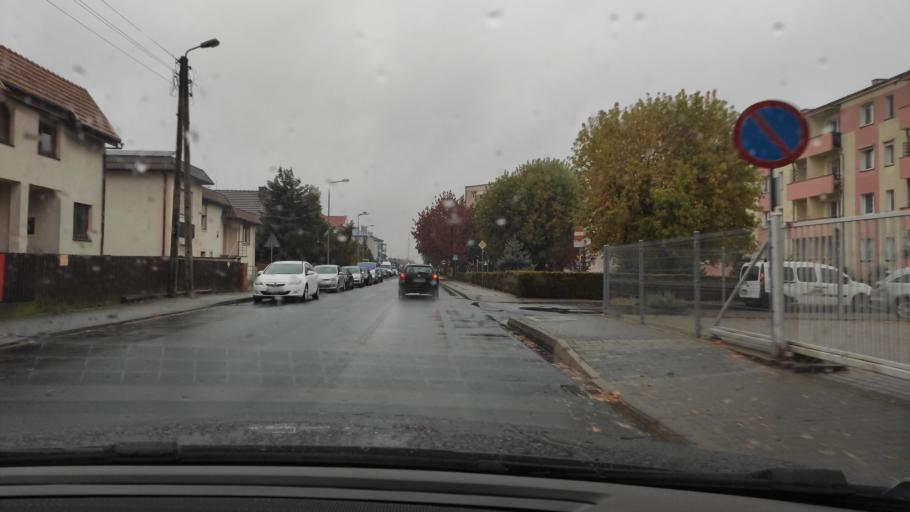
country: PL
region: Greater Poland Voivodeship
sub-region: Powiat poznanski
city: Kornik
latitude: 52.2524
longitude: 17.0900
